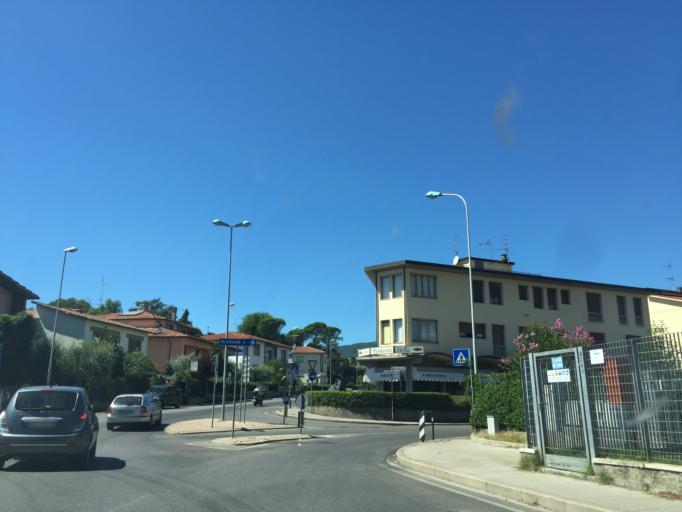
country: IT
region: Tuscany
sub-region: Provincia di Pistoia
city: Pistoia
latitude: 43.9443
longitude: 10.9112
